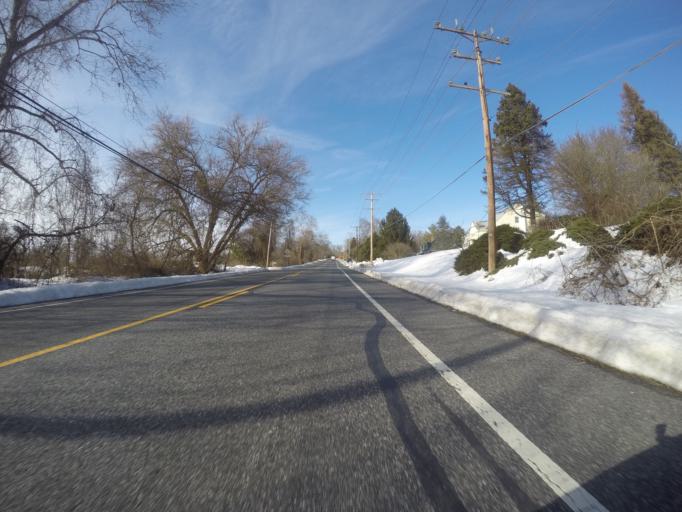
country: US
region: Maryland
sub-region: Baltimore County
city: Hunt Valley
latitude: 39.5432
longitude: -76.6501
